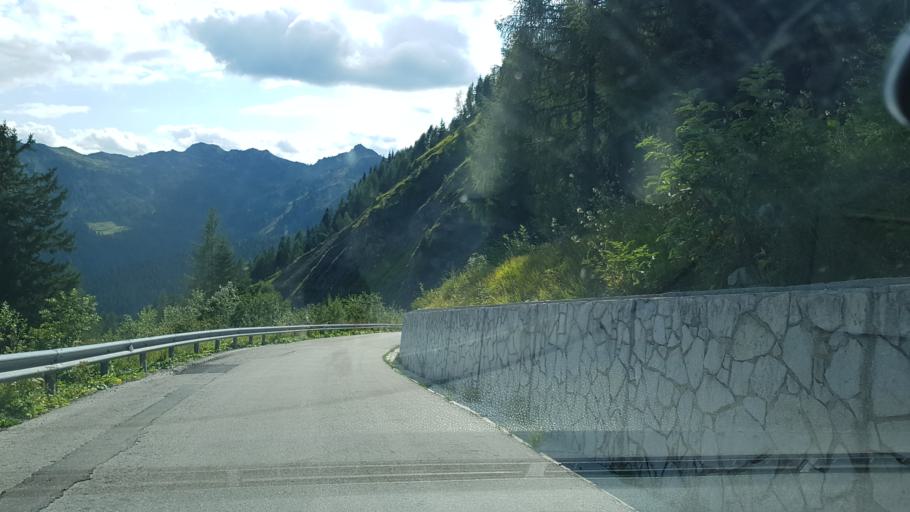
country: IT
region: Friuli Venezia Giulia
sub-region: Provincia di Udine
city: Sauris di Sotto
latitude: 46.4738
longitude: 12.6455
